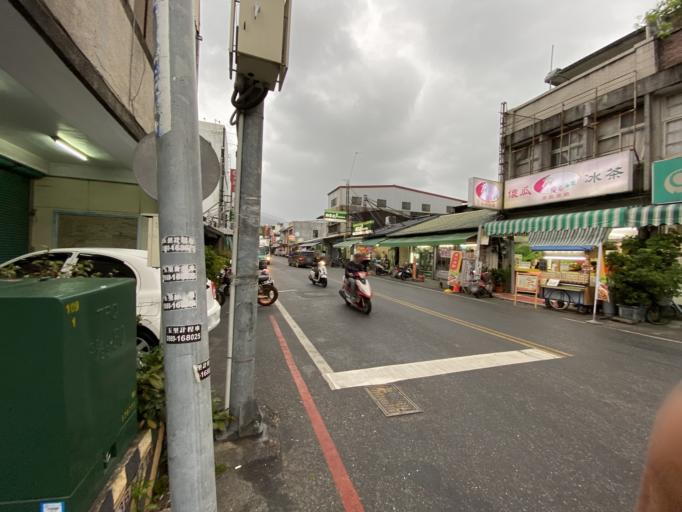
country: TW
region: Taiwan
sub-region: Taitung
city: Taitung
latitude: 23.3342
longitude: 121.3146
